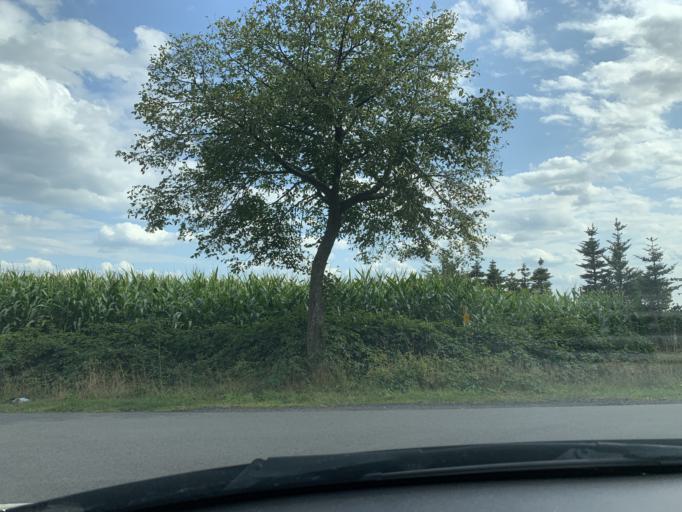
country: DE
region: Lower Saxony
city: Westerstede
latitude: 53.2538
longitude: 7.8850
